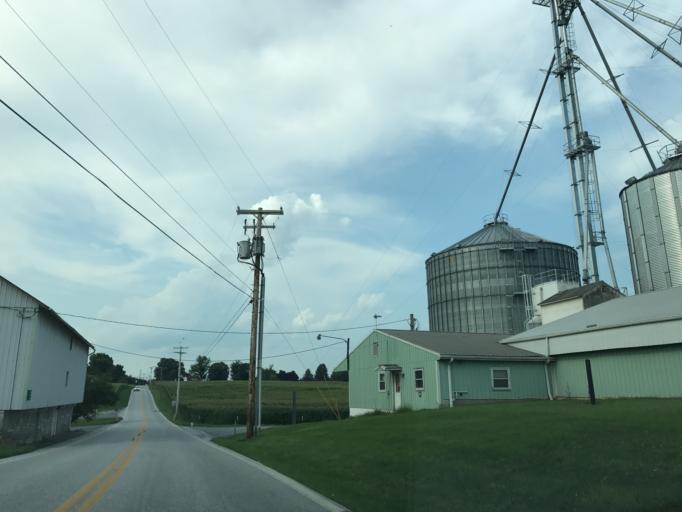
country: US
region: Pennsylvania
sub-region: Lancaster County
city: Mount Joy
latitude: 40.1033
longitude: -76.5333
